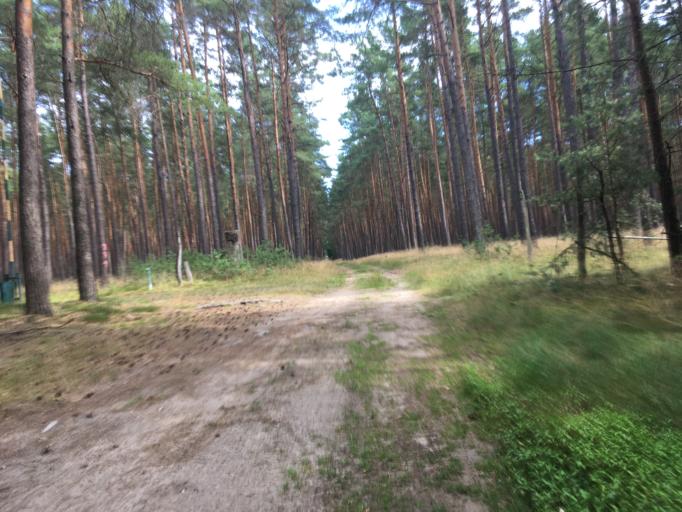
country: DE
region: Brandenburg
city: Rheinsberg
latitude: 53.0318
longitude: 12.9327
